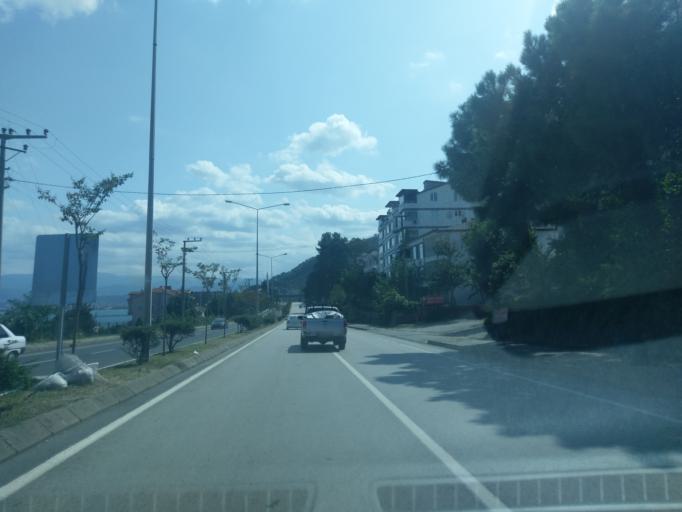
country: TR
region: Ordu
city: Ordu
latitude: 41.0073
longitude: 37.8691
